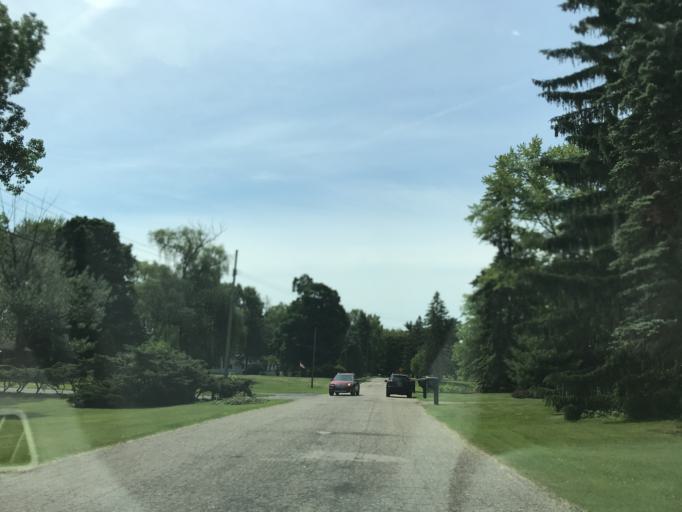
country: US
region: Michigan
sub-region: Oakland County
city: Bingham Farms
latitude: 42.4762
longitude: -83.2708
